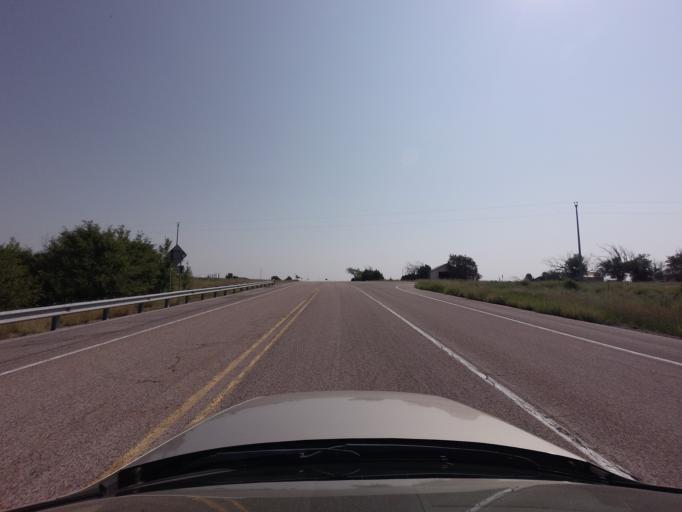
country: US
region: New Mexico
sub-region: Quay County
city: Tucumcari
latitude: 34.8225
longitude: -103.7427
